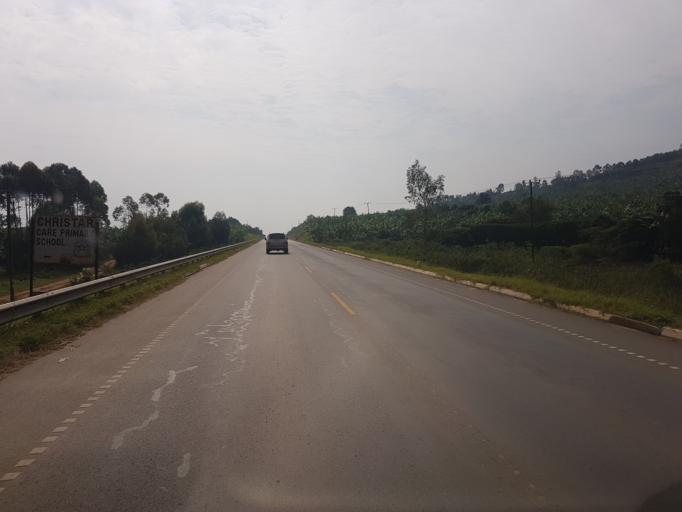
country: UG
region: Western Region
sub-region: Sheema District
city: Kibingo
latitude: -0.6389
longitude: 30.5110
